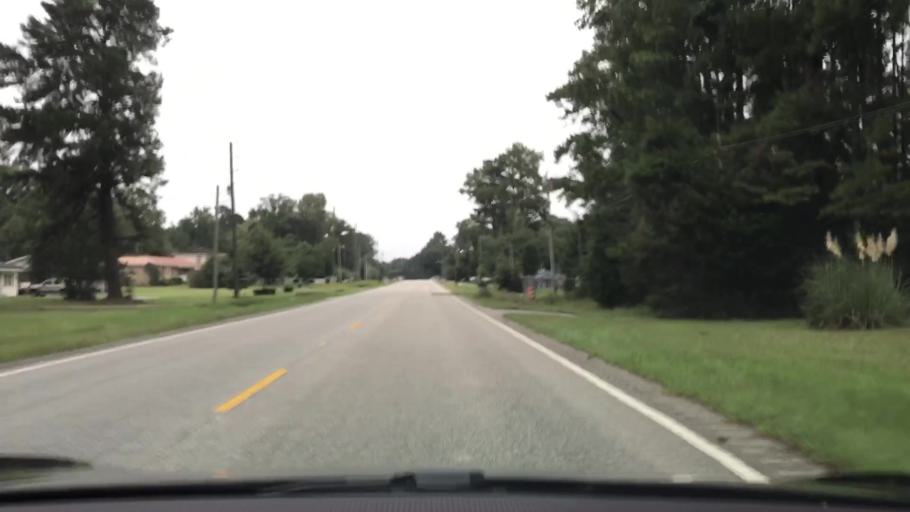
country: US
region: Alabama
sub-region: Coffee County
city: Elba
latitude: 31.3870
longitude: -86.0852
